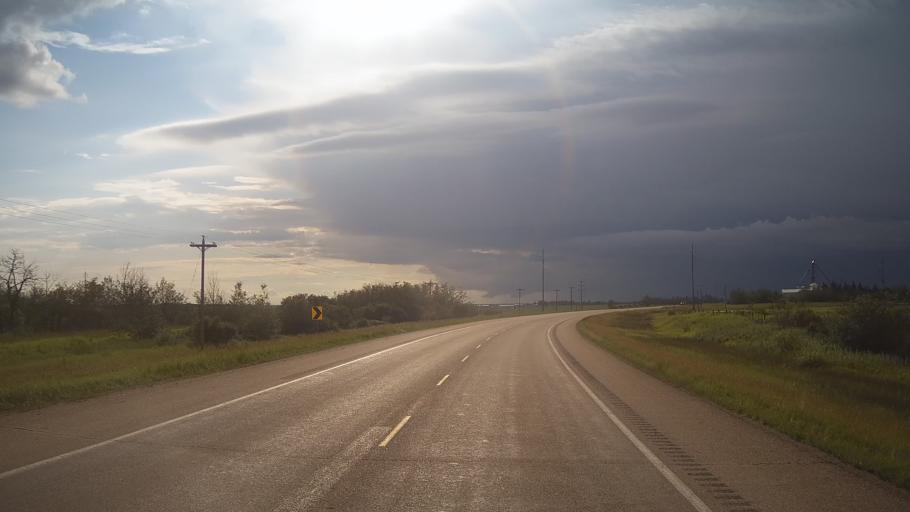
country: CA
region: Alberta
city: Vegreville
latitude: 53.2218
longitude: -112.2170
